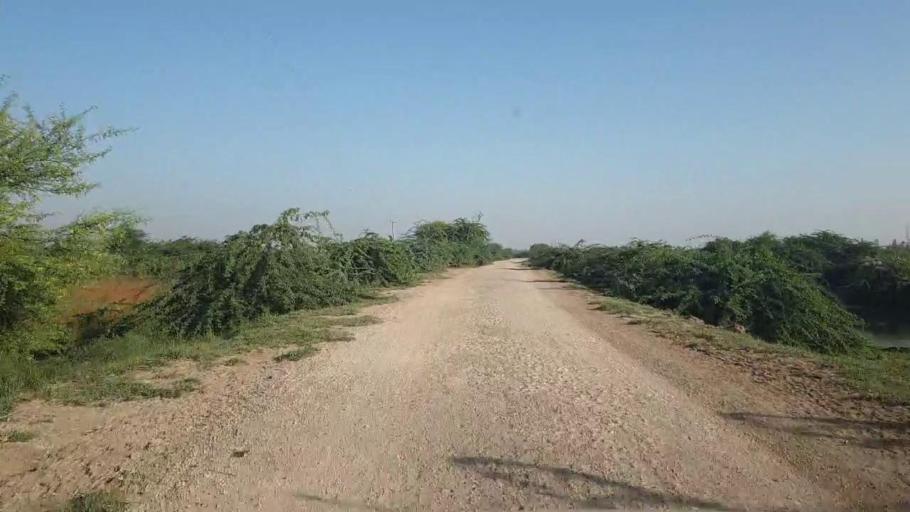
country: PK
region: Sindh
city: Badin
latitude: 24.6947
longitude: 68.8160
